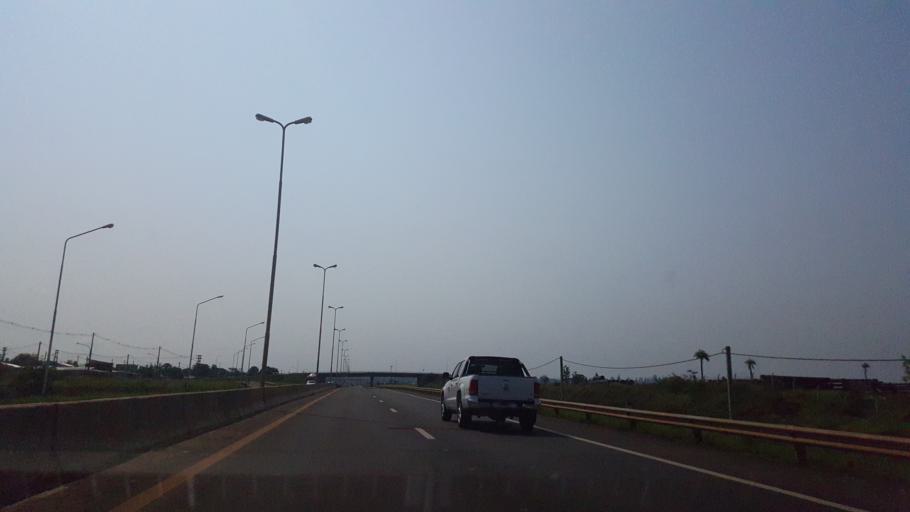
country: AR
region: Misiones
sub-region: Departamento de Capital
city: Posadas
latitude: -27.4272
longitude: -55.8717
